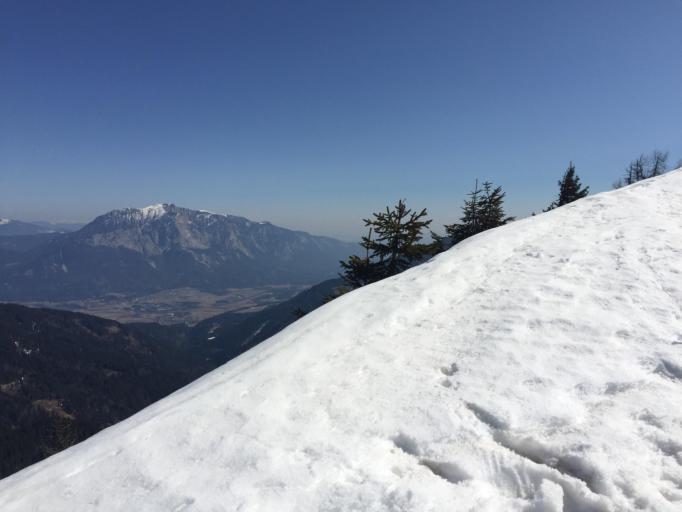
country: IT
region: Friuli Venezia Giulia
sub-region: Provincia di Udine
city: Tarvisio
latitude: 46.5472
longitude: 13.5193
